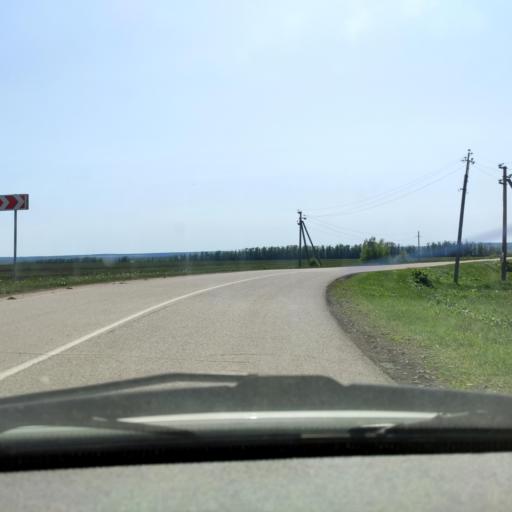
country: RU
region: Bashkortostan
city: Avdon
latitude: 54.5537
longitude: 55.6672
